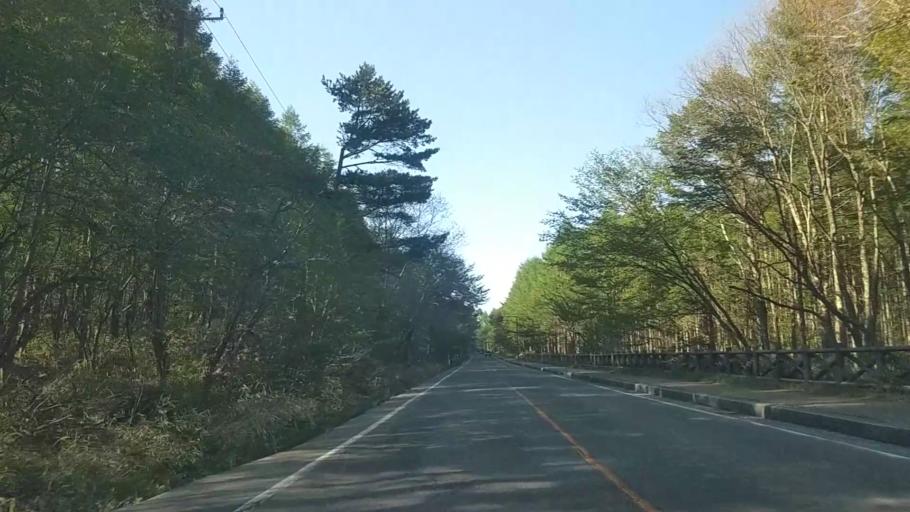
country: JP
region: Yamanashi
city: Nirasaki
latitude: 35.9172
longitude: 138.4050
